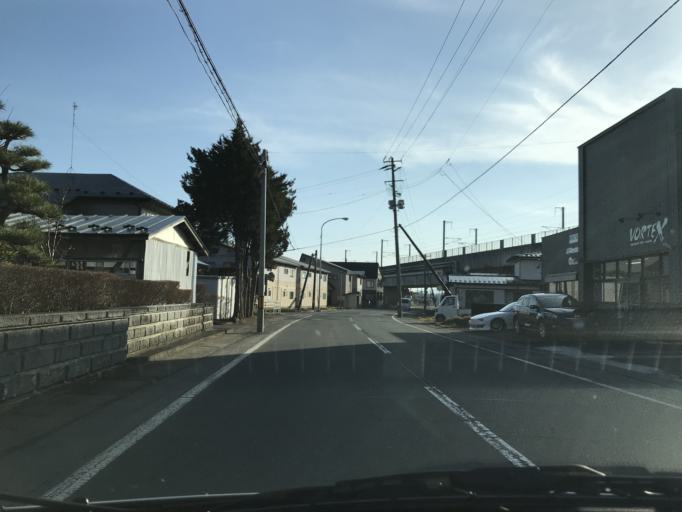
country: JP
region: Iwate
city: Kitakami
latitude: 39.2588
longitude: 141.1132
